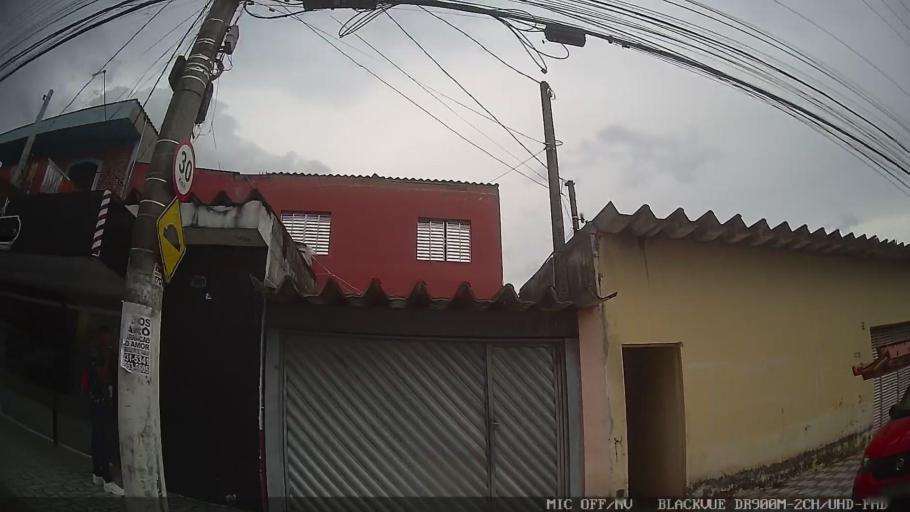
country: BR
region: Sao Paulo
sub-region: Suzano
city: Suzano
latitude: -23.5588
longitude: -46.2925
